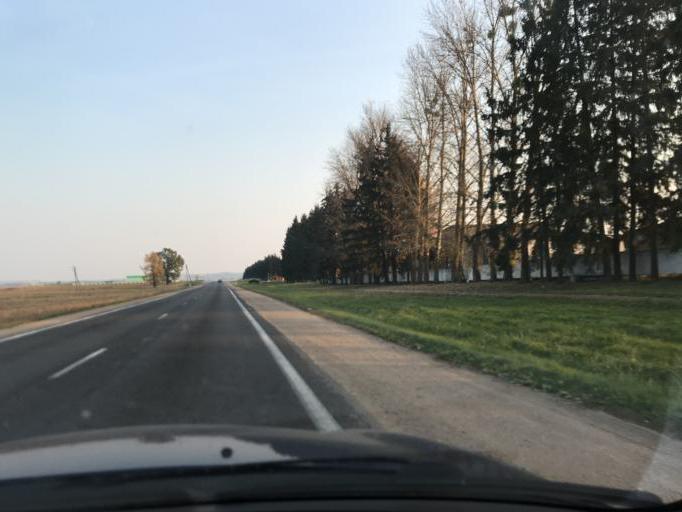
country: BY
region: Grodnenskaya
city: Karelichy
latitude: 53.5567
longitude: 26.1550
